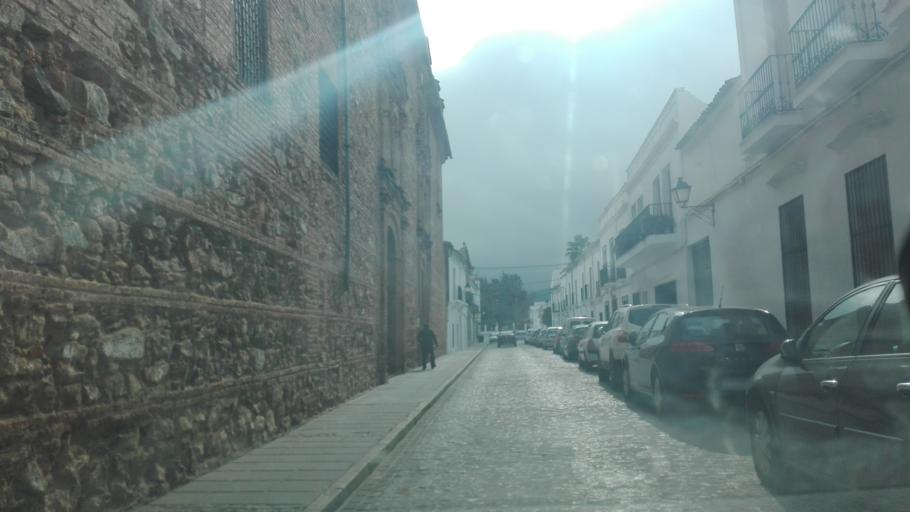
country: ES
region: Extremadura
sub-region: Provincia de Badajoz
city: Llerena
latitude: 38.2365
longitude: -6.0137
